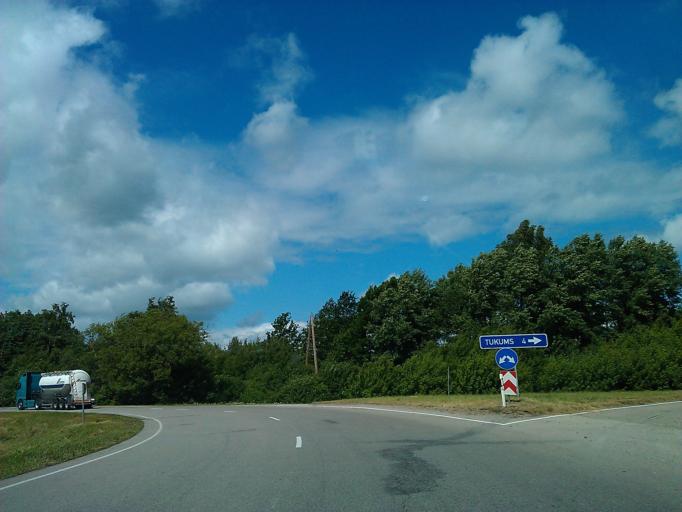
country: LV
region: Tukuma Rajons
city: Tukums
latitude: 56.9496
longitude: 23.1154
